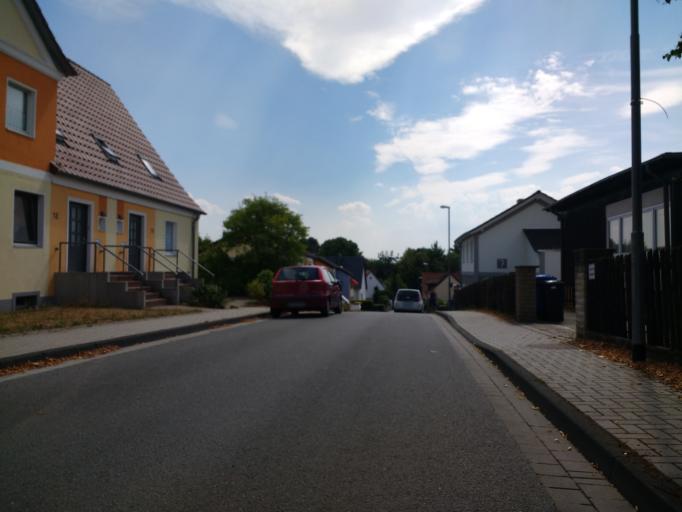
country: DE
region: Lower Saxony
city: Gifhorn
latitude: 52.4881
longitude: 10.5373
